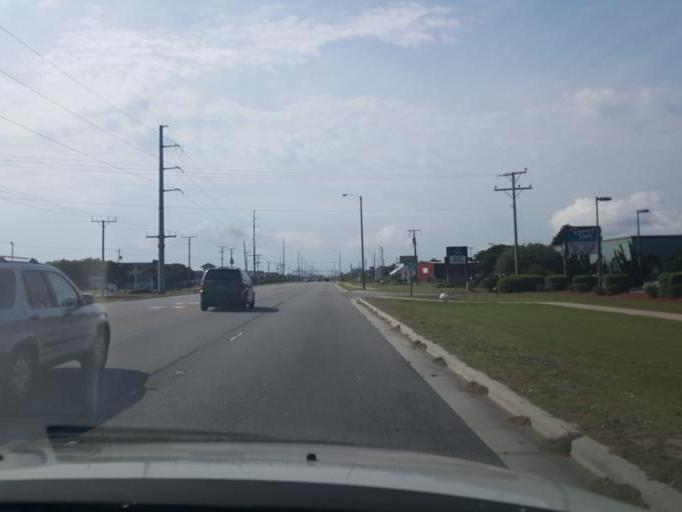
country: US
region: North Carolina
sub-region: Dare County
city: Kill Devil Hills
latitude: 36.0081
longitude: -75.6577
